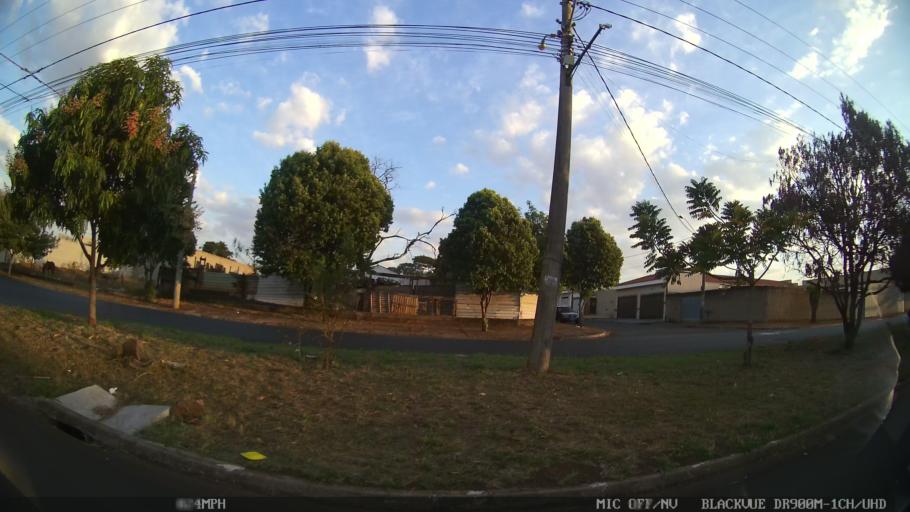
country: BR
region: Sao Paulo
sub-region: Ribeirao Preto
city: Ribeirao Preto
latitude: -21.1529
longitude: -47.7587
